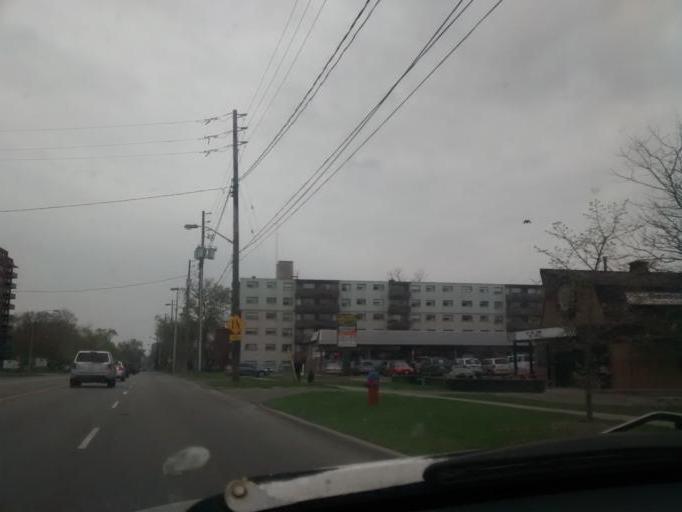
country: CA
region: Ontario
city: Burlington
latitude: 43.3378
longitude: -79.7860
